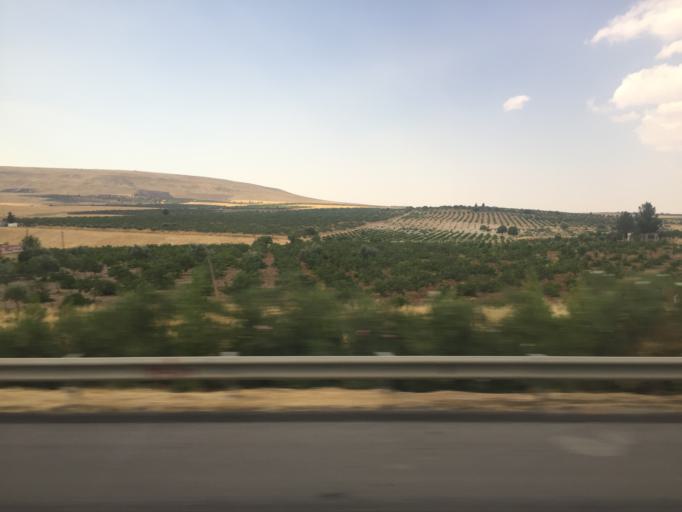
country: TR
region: Sanliurfa
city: Akziyaret
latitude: 37.2667
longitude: 38.7793
